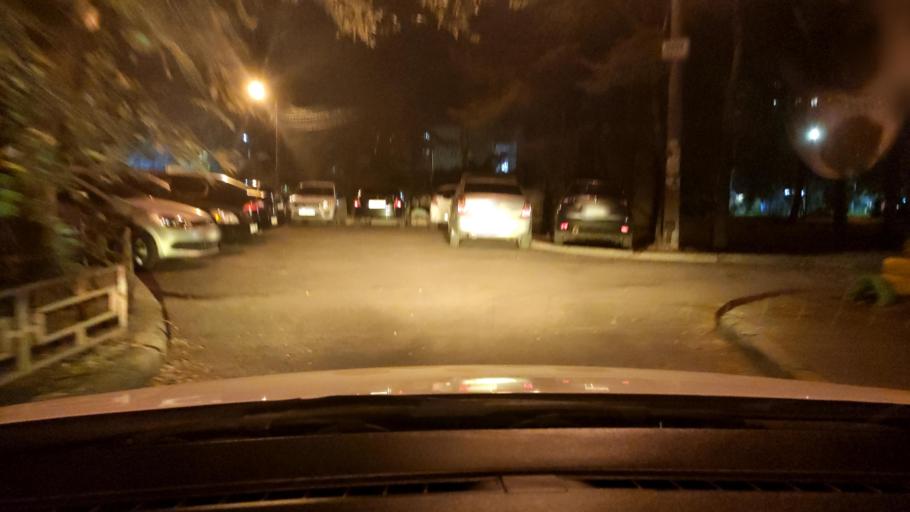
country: RU
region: Voronezj
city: Pridonskoy
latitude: 51.6535
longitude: 39.1106
